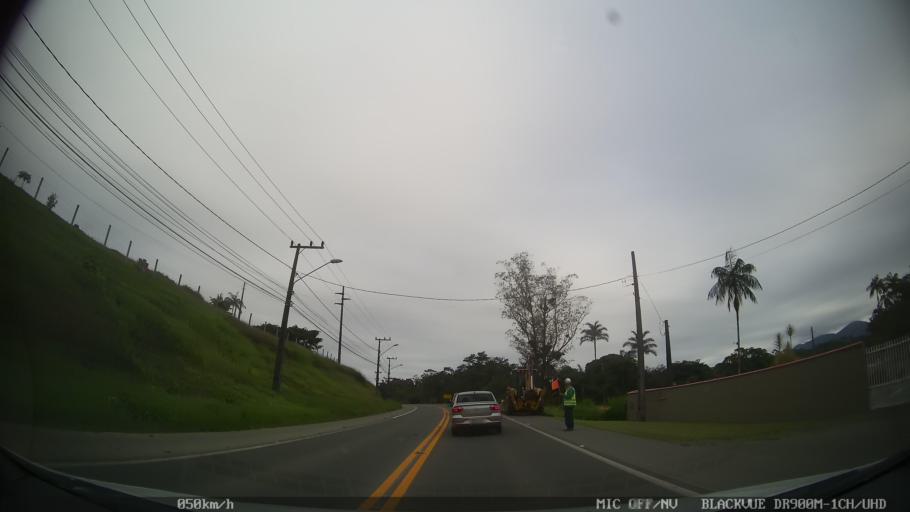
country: BR
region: Santa Catarina
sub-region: Joinville
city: Joinville
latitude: -26.3011
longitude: -48.9203
